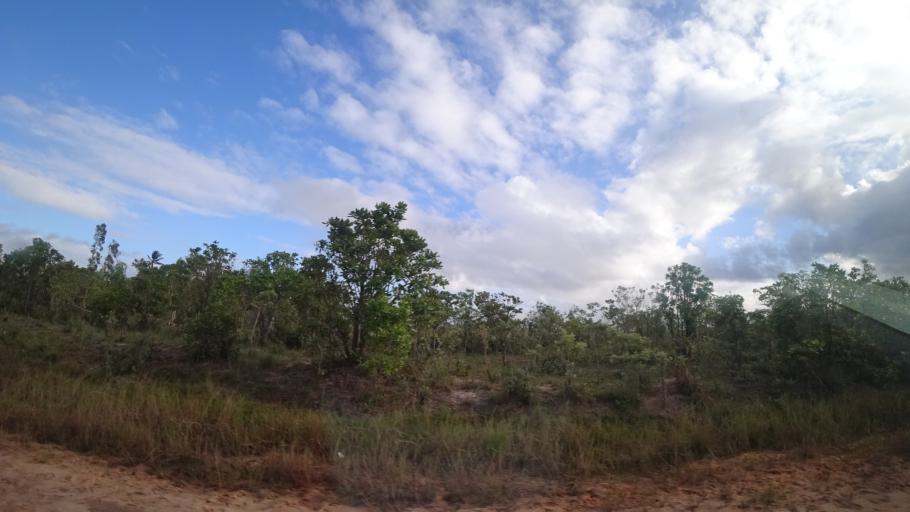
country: MZ
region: Sofala
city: Beira
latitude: -19.6805
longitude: 35.0574
